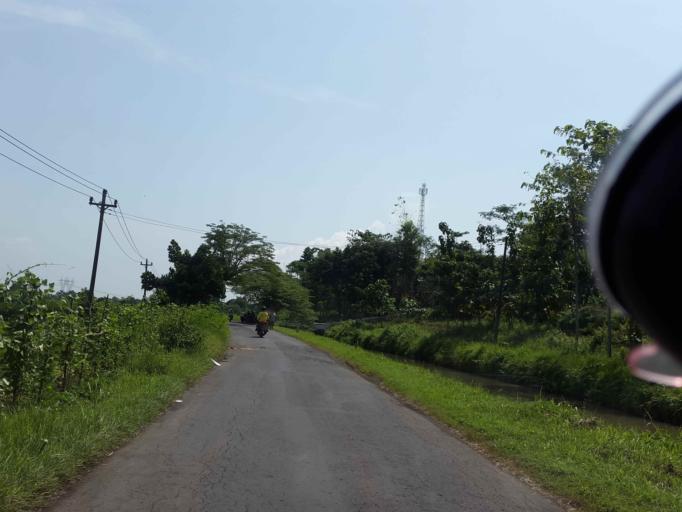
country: ID
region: Central Java
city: Pemalang
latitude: -6.9462
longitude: 109.3839
